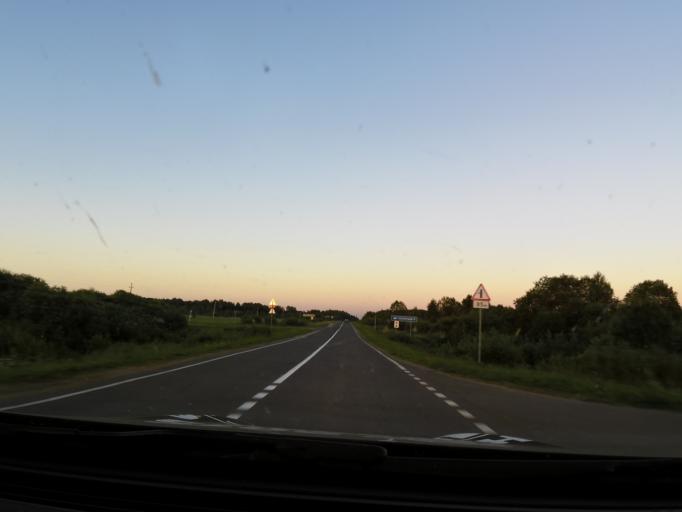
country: RU
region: Jaroslavl
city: Lyubim
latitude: 58.3390
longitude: 40.8703
